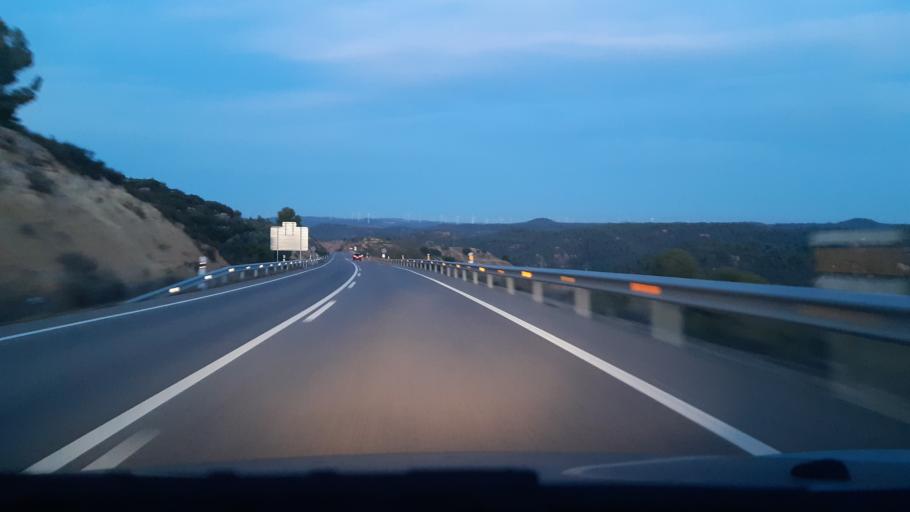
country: ES
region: Aragon
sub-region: Provincia de Teruel
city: Calaceite
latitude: 41.0195
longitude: 0.2096
